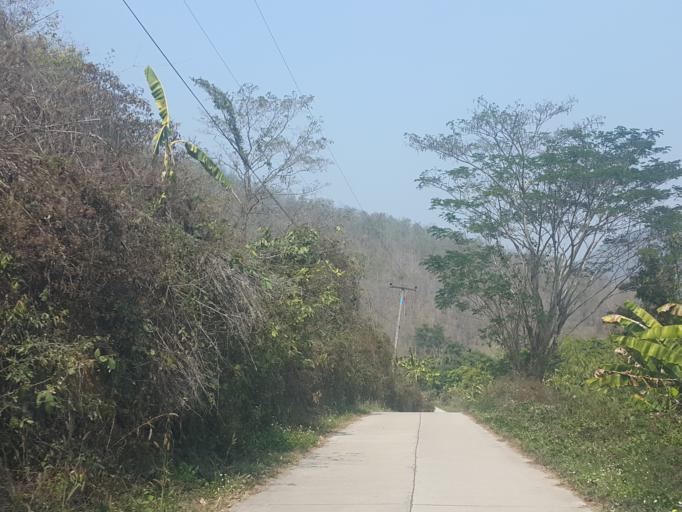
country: TH
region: Chiang Mai
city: Hang Dong
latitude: 18.7395
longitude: 98.8261
